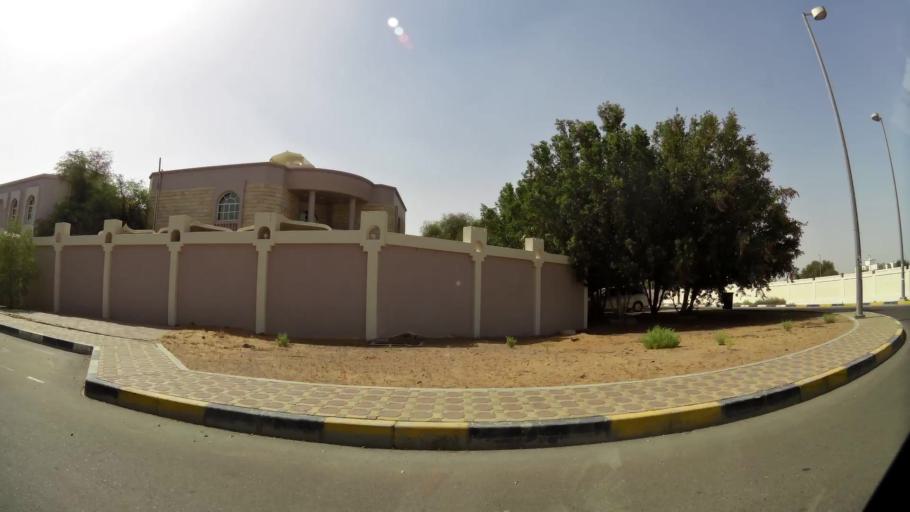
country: AE
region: Abu Dhabi
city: Al Ain
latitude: 24.2328
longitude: 55.6862
